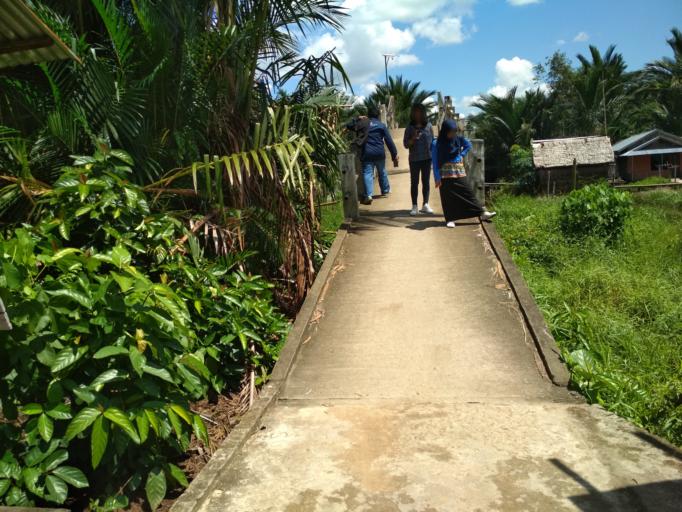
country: ID
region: West Kalimantan
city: Pontianak
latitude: -0.1326
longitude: 109.4461
